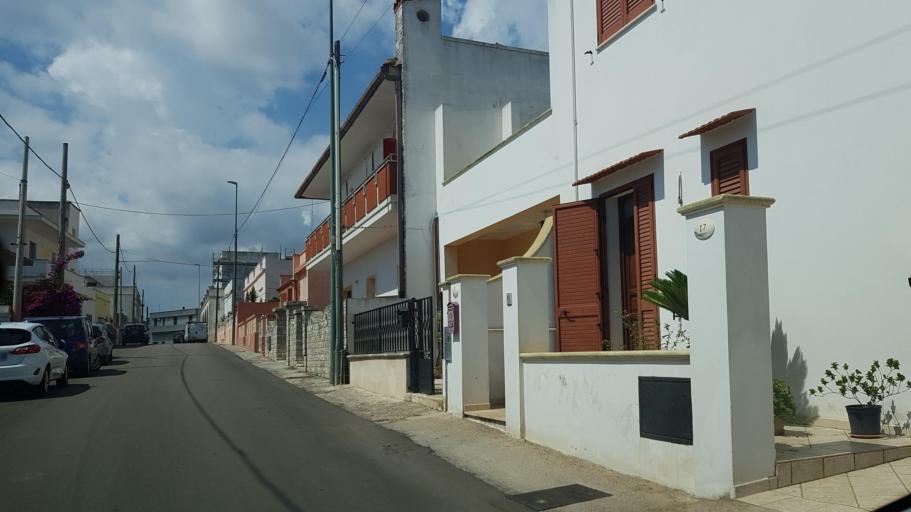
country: IT
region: Apulia
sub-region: Provincia di Lecce
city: Castrignano del Capo
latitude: 39.8305
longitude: 18.3529
